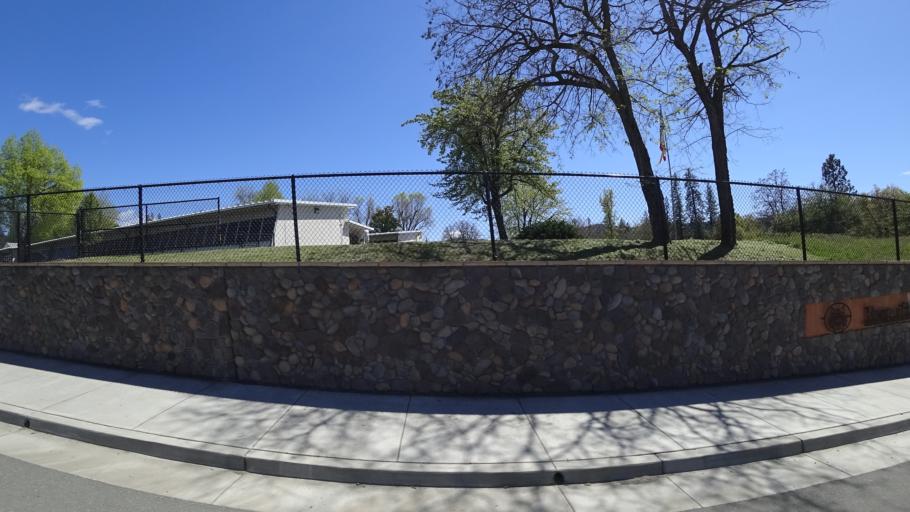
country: US
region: California
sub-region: Trinity County
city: Weaverville
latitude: 40.7334
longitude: -122.9376
